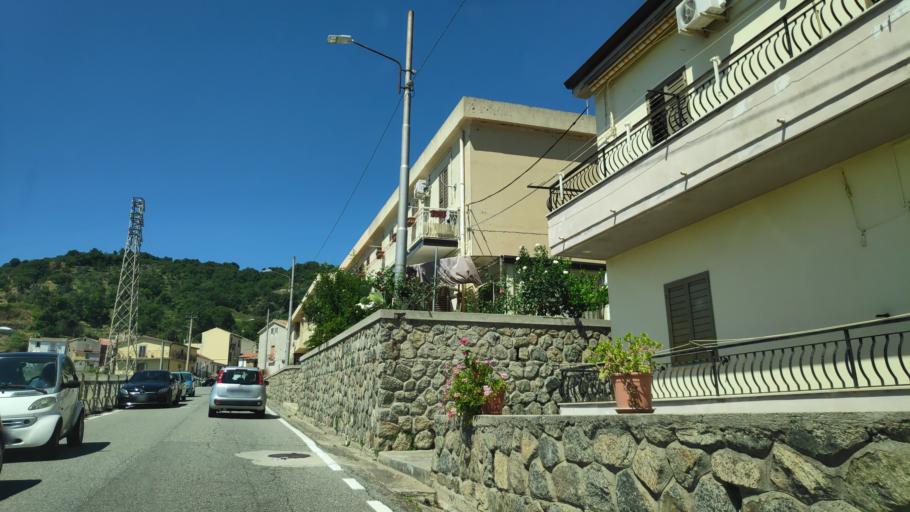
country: IT
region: Calabria
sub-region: Provincia di Catanzaro
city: Montauro
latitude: 38.7476
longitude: 16.5145
